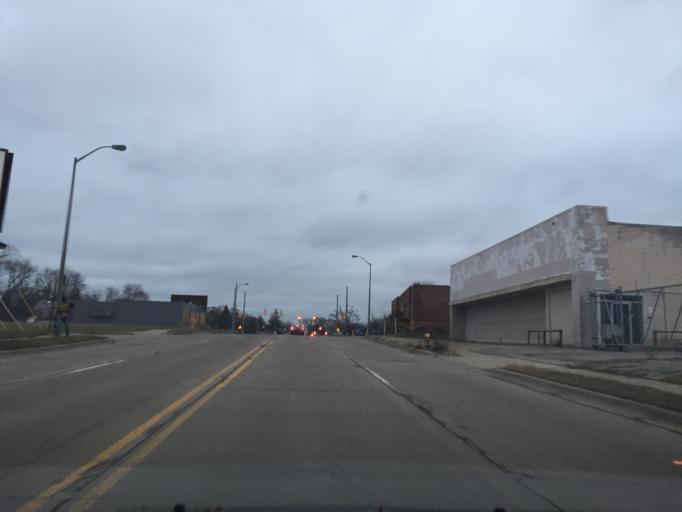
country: US
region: Michigan
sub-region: Oakland County
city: Pontiac
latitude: 42.6345
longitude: -83.2768
